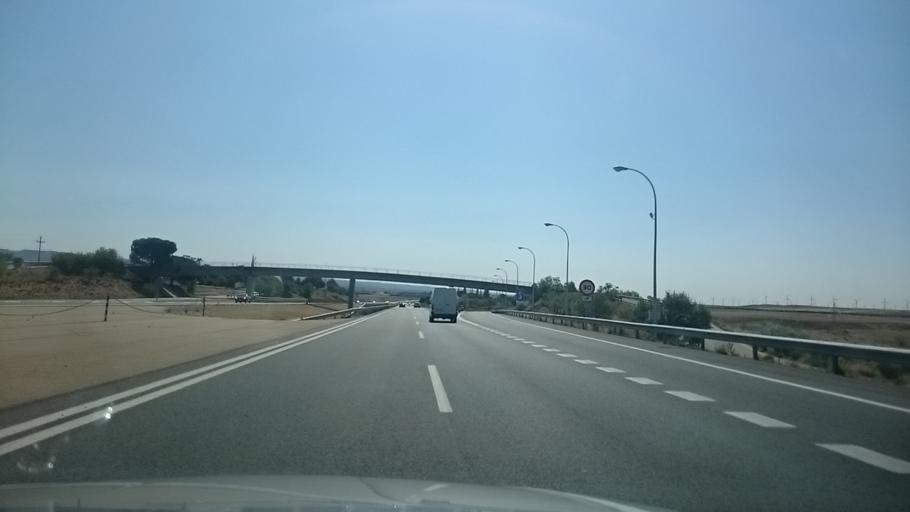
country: ES
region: Aragon
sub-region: Provincia de Zaragoza
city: Gallur
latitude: 41.8346
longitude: -1.3255
